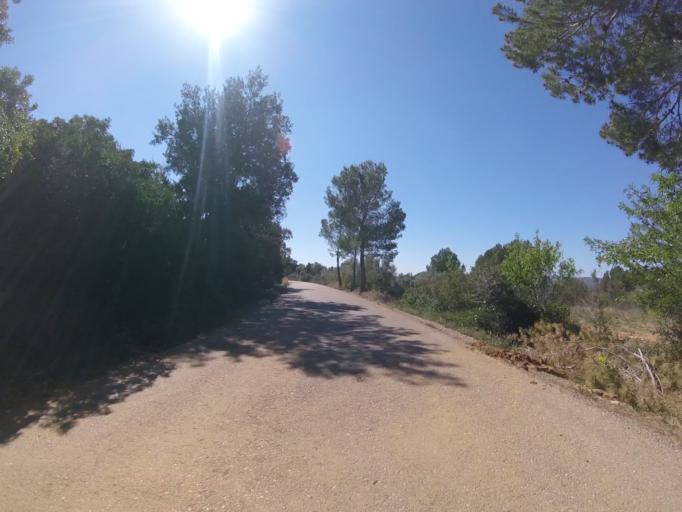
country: ES
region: Valencia
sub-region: Provincia de Castello
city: Cuevas de Vinroma
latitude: 40.3947
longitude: 0.1627
